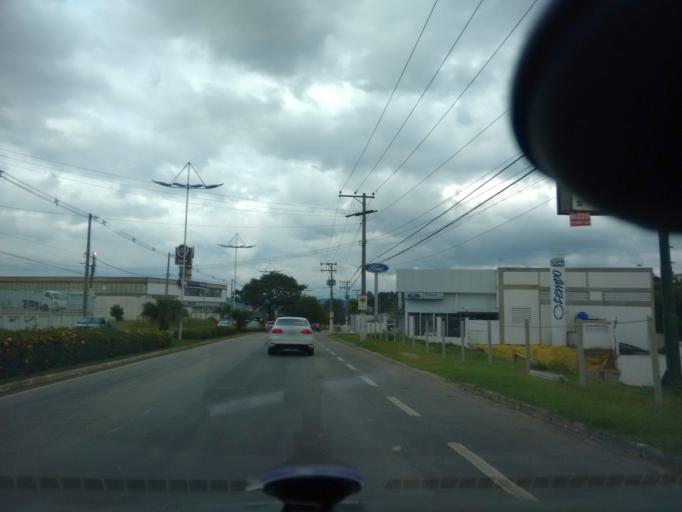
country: BR
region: Sao Paulo
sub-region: Indaiatuba
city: Indaiatuba
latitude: -23.0862
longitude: -47.1821
